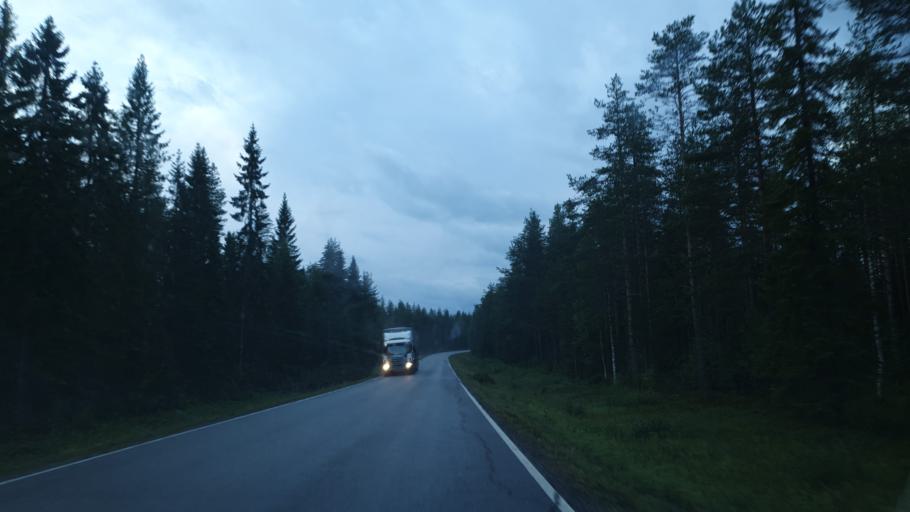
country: FI
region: Kainuu
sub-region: Kehys-Kainuu
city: Kuhmo
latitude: 63.9579
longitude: 29.7052
